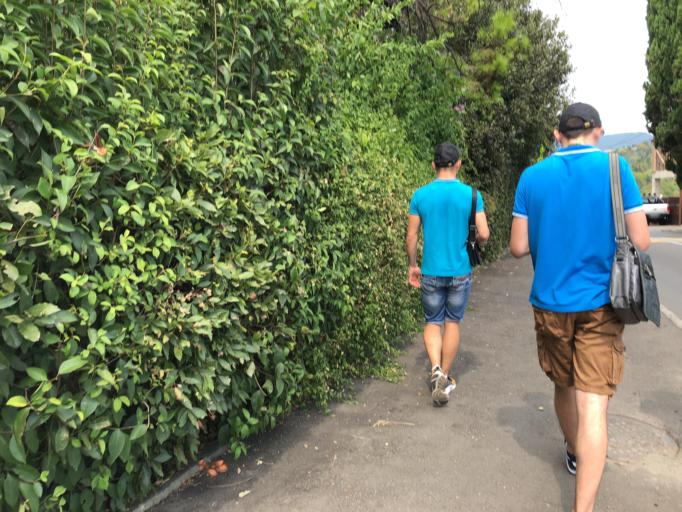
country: RU
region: Krasnodarskiy
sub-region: Sochi City
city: Sochi
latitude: 43.5916
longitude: 39.7407
